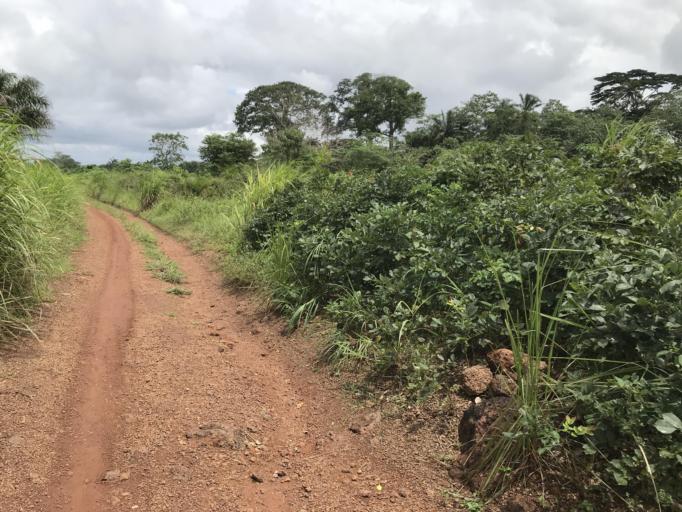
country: SL
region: Eastern Province
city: Buedu
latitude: 8.4700
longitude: -10.3276
